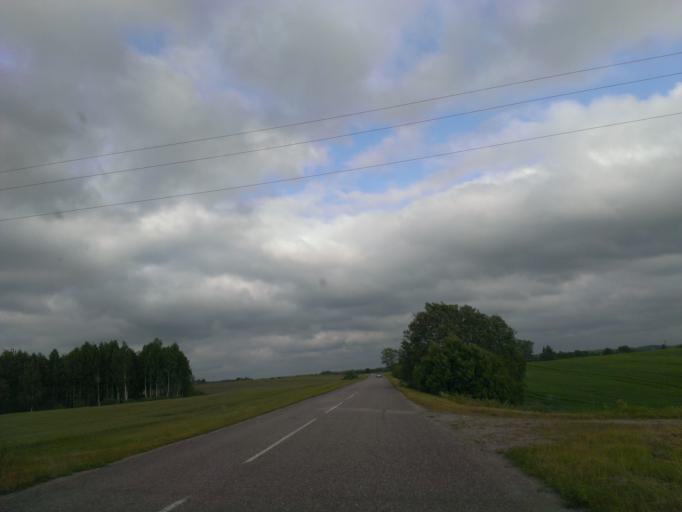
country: LV
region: Aizpute
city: Aizpute
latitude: 56.7029
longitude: 21.7763
